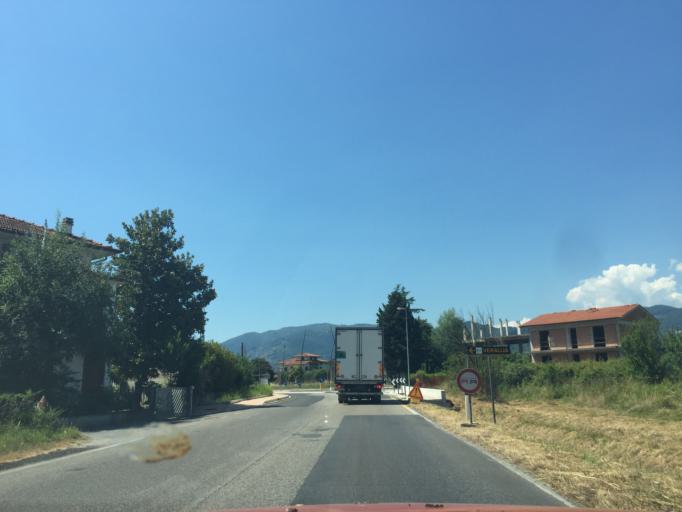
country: IT
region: Tuscany
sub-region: Provincia di Pistoia
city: Santa Lucia
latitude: 43.8726
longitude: 10.6936
